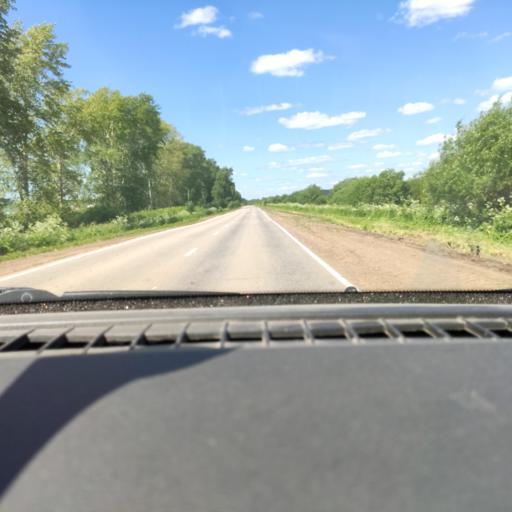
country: RU
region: Perm
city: Chaykovskaya
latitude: 58.0996
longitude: 55.5924
